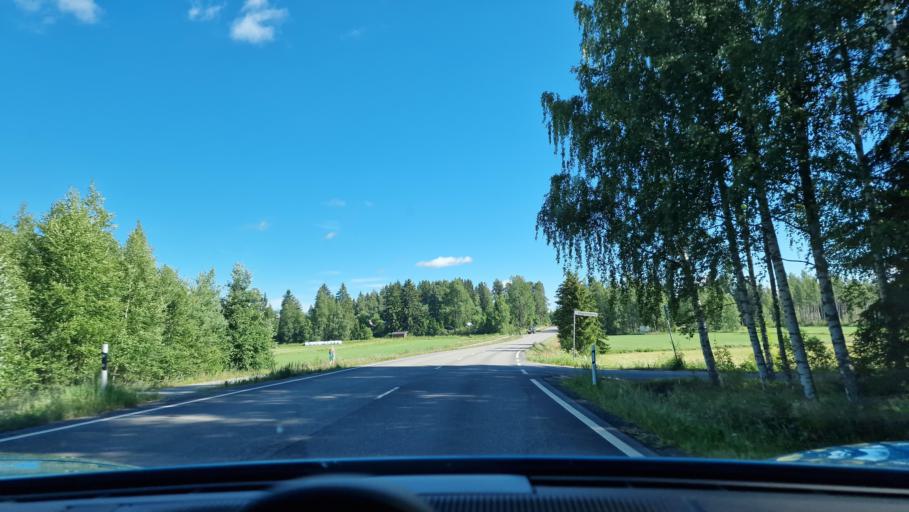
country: FI
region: Pirkanmaa
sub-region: Tampere
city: Kangasala
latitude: 61.4877
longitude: 24.1562
